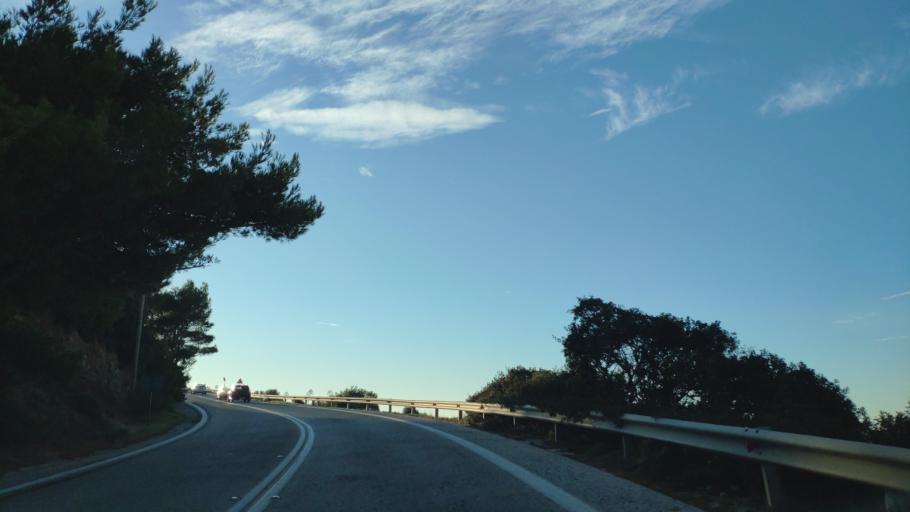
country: GR
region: Attica
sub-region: Nomarchia Anatolikis Attikis
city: Palaia Fokaia
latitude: 37.6775
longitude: 23.9438
